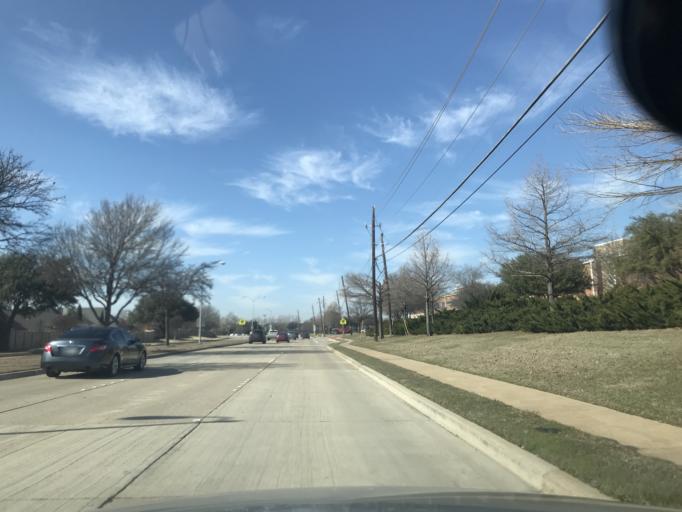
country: US
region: Texas
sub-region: Dallas County
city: Addison
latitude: 33.0433
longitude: -96.8145
